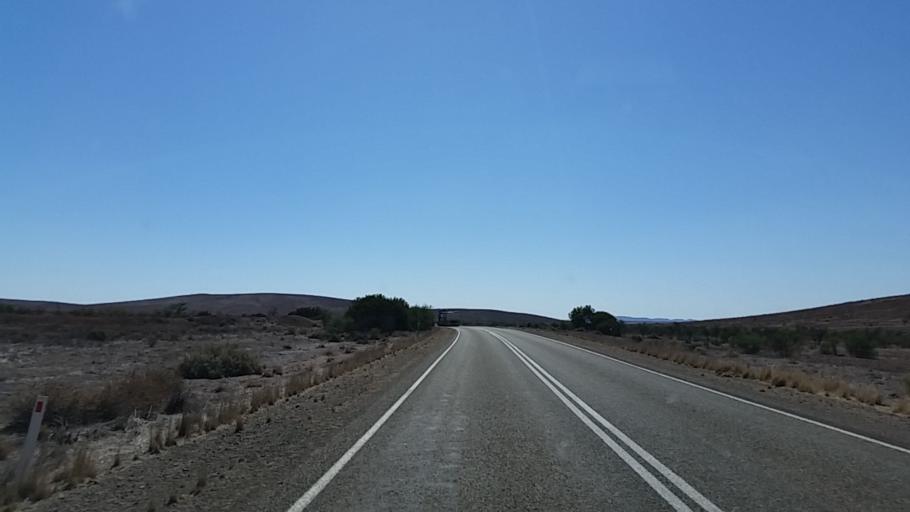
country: AU
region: South Australia
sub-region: Flinders Ranges
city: Quorn
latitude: -32.1431
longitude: 138.5191
